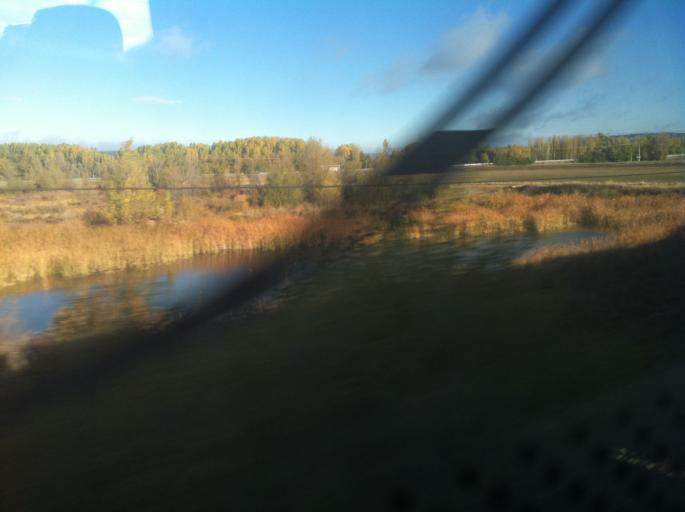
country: ES
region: Castille and Leon
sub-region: Provincia de Palencia
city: Cordovilla la Real
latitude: 42.0377
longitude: -4.2649
